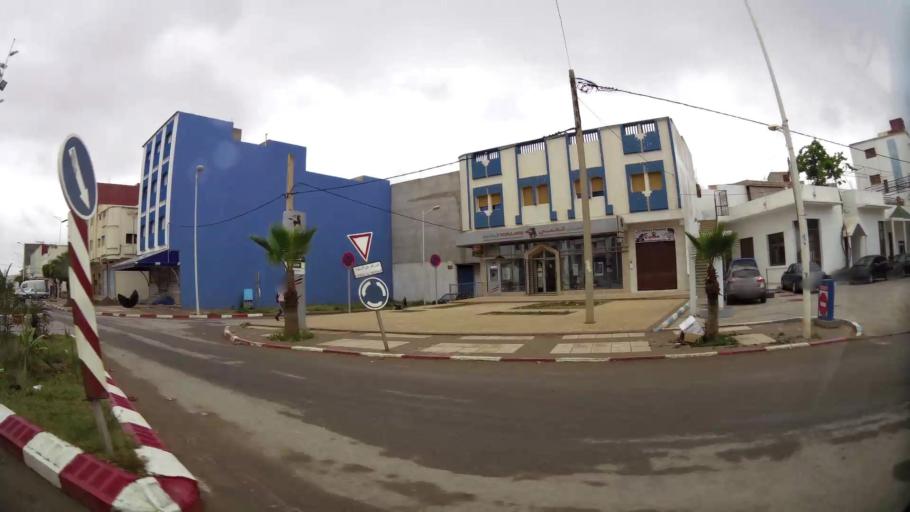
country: MA
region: Oriental
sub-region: Nador
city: Midar
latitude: 35.0478
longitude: -3.4568
